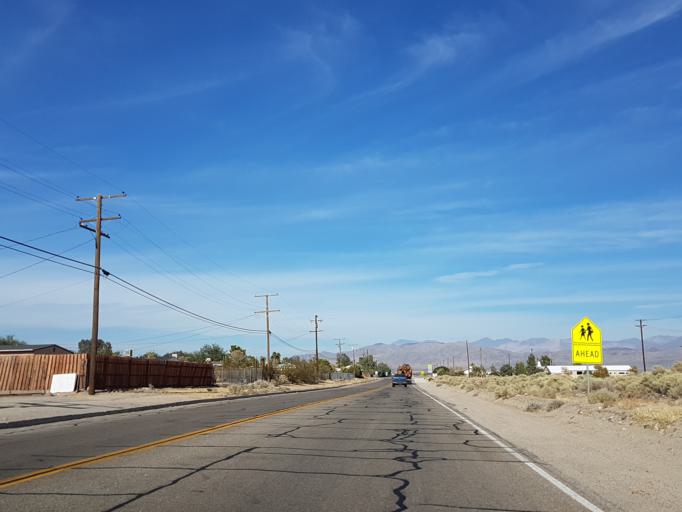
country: US
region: California
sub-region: San Bernardino County
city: Searles Valley
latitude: 35.7887
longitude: -117.3600
